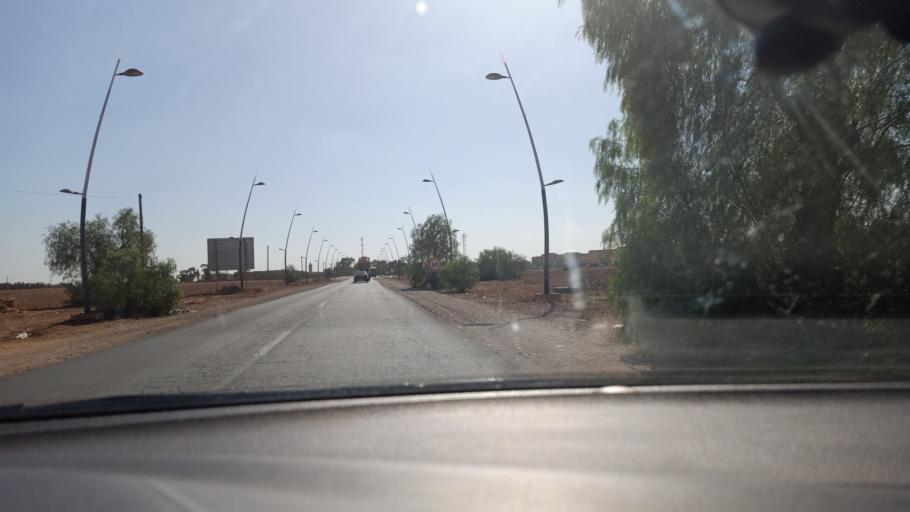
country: MA
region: Doukkala-Abda
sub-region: Safi
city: Youssoufia
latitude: 32.0874
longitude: -8.6186
